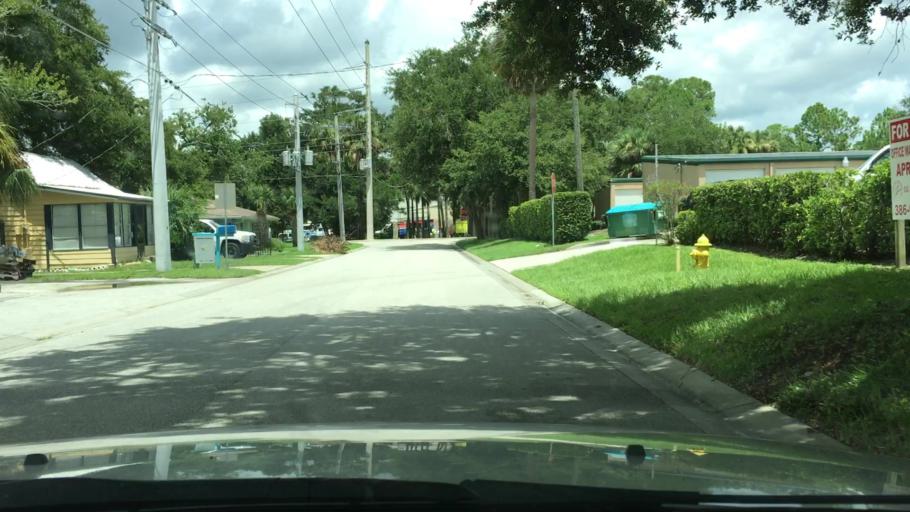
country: US
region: Florida
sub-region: Volusia County
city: Ormond Beach
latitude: 29.2733
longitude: -81.0604
